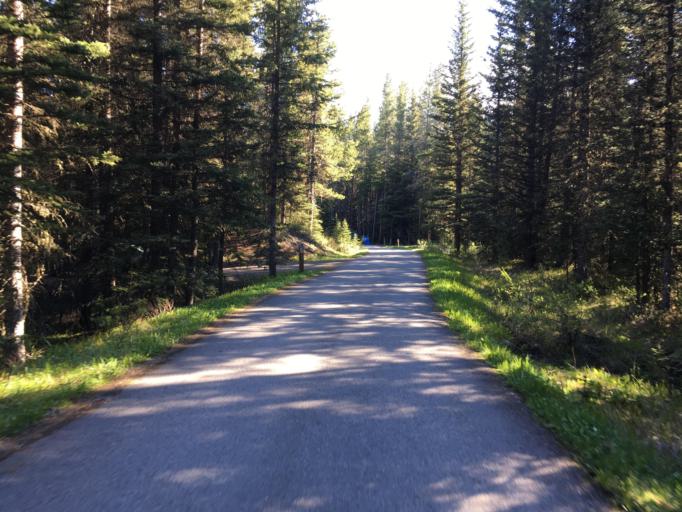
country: CA
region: Alberta
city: Canmore
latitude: 50.6297
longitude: -115.1043
